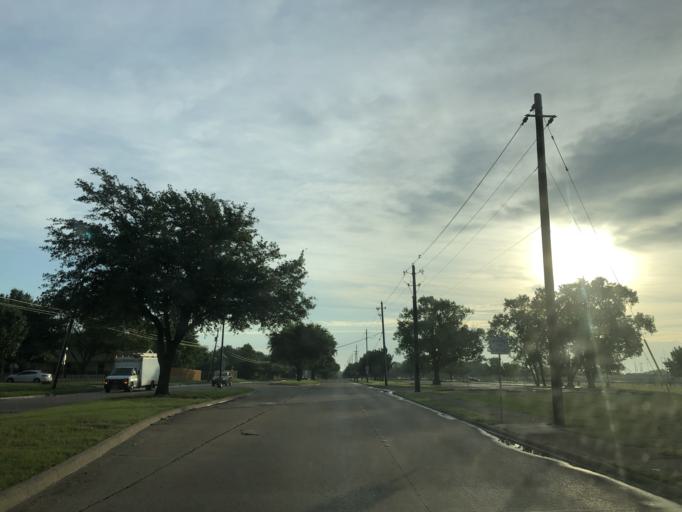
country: US
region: Texas
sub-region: Dallas County
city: Garland
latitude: 32.8437
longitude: -96.6221
